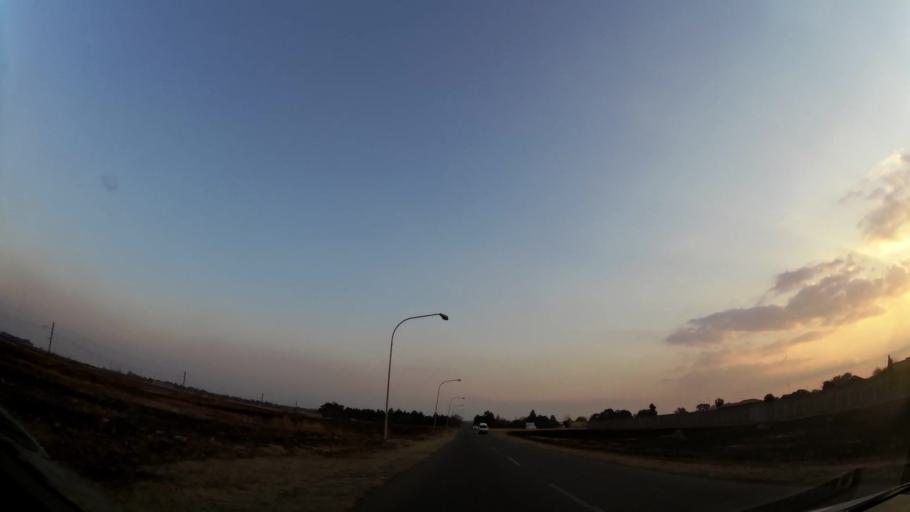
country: ZA
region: Gauteng
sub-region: Ekurhuleni Metropolitan Municipality
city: Springs
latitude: -26.3313
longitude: 28.4412
